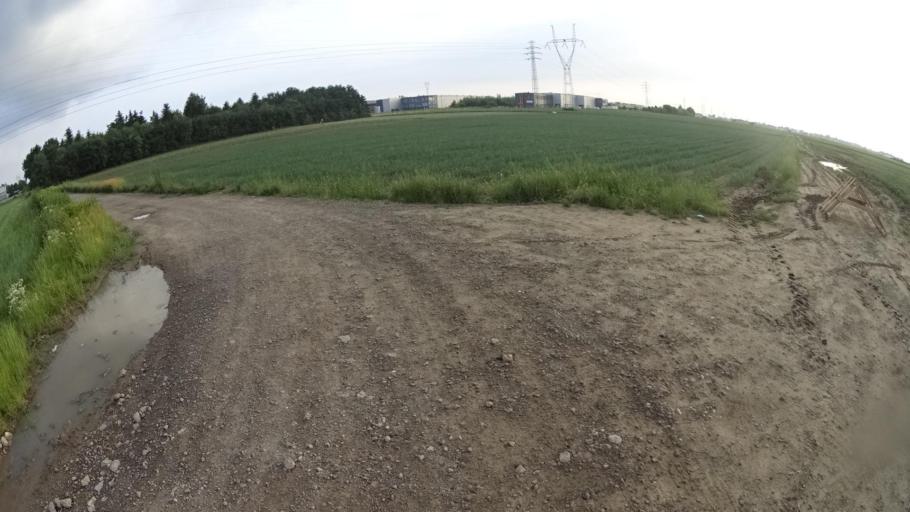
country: PL
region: Masovian Voivodeship
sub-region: Powiat warszawski zachodni
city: Babice
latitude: 52.2219
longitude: 20.8552
